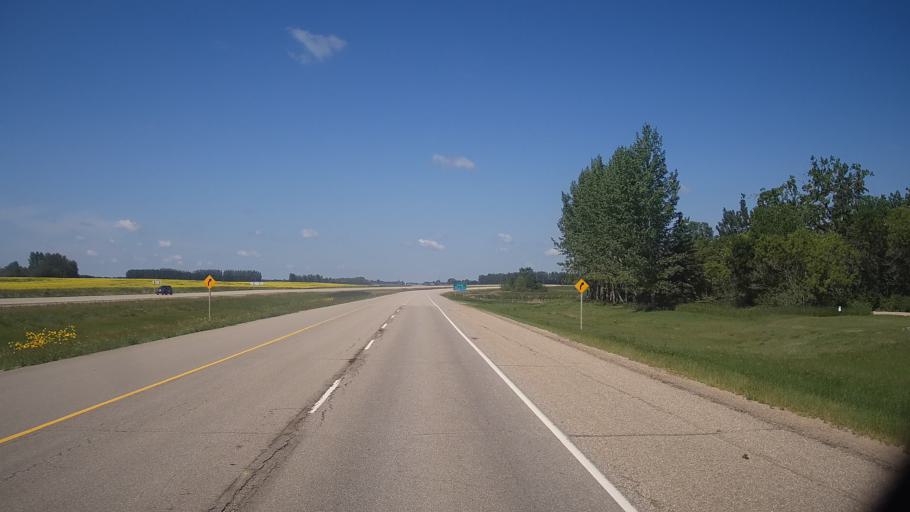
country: CA
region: Saskatchewan
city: Saskatoon
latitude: 51.9982
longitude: -106.3149
